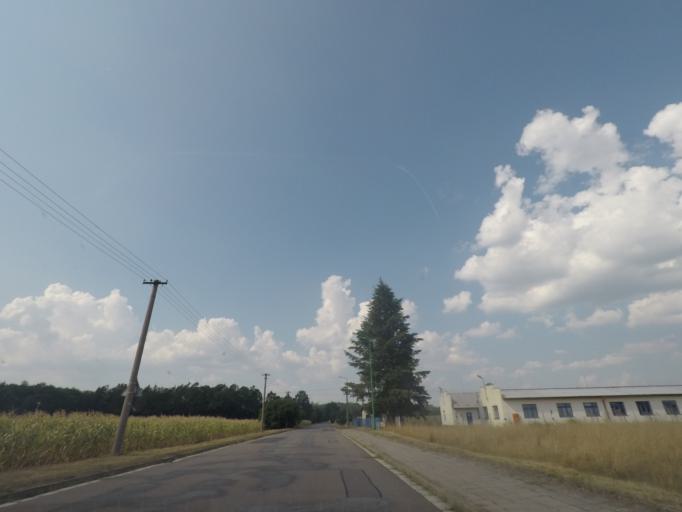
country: CZ
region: Pardubicky
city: Horni Jeleni
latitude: 50.0550
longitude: 16.0830
